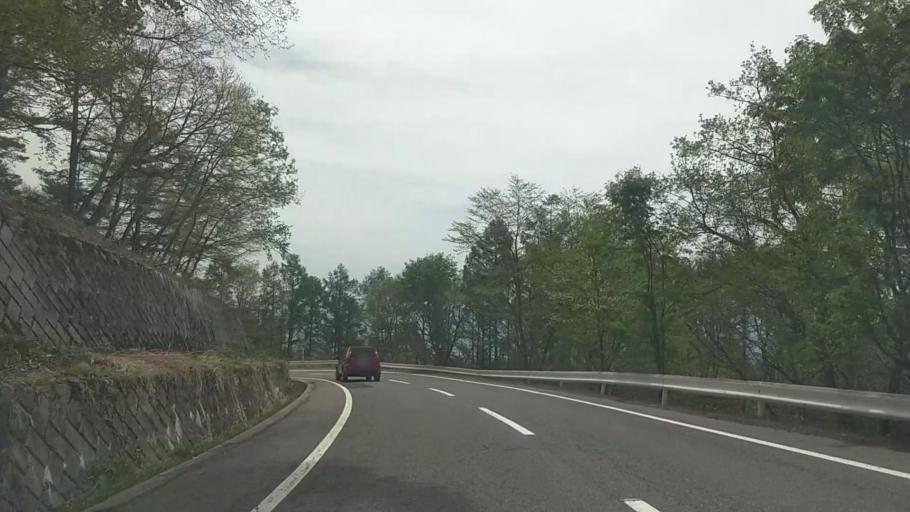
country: JP
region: Nagano
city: Chino
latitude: 36.0414
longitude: 138.2814
